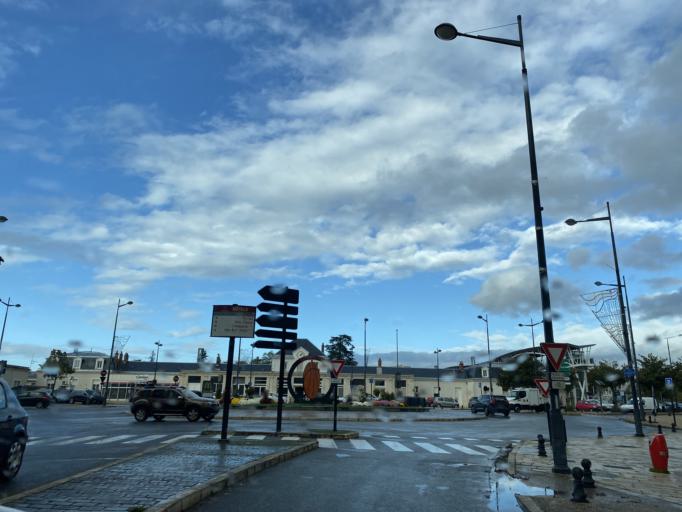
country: FR
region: Centre
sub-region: Departement du Cher
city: Bourges
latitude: 47.0932
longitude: 2.3941
